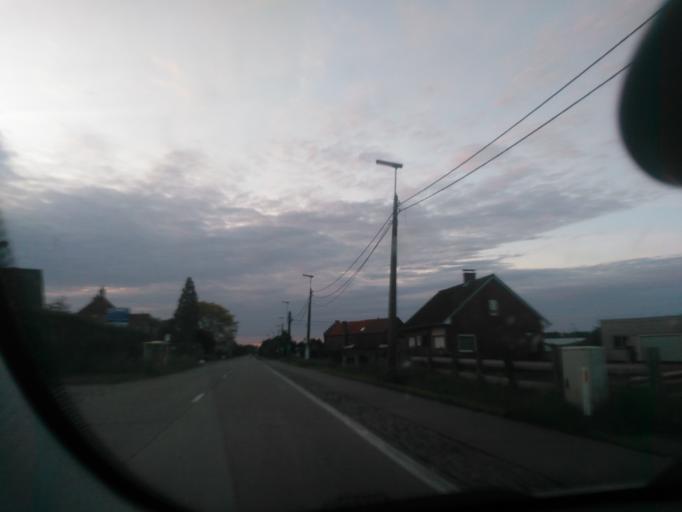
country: BE
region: Flanders
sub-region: Provincie Oost-Vlaanderen
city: Sint-Gillis-Waas
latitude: 51.2749
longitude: 4.1842
